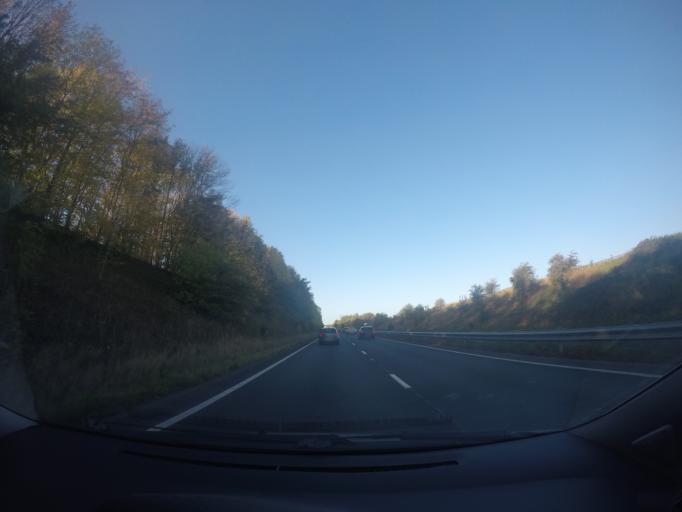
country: GB
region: England
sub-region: North Yorkshire
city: Tadcaster
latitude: 53.8711
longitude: -1.2838
